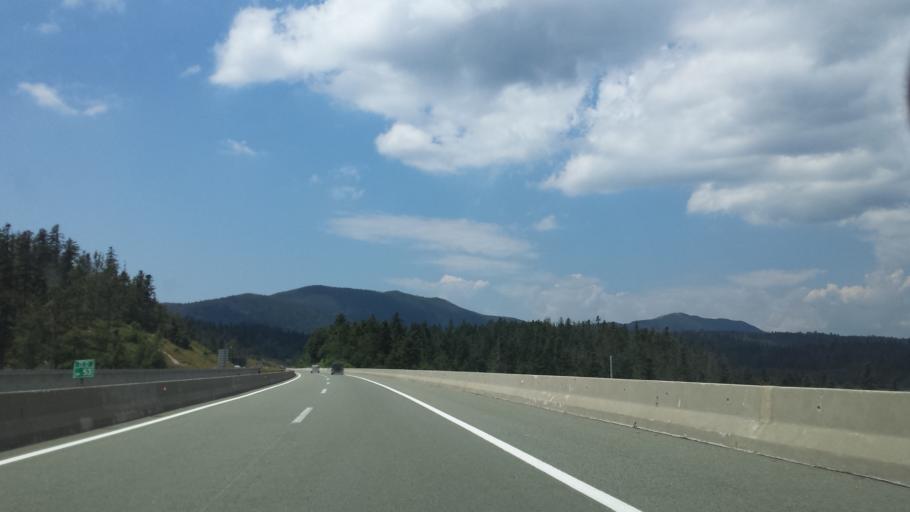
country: HR
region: Primorsko-Goranska
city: Hreljin
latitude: 45.3168
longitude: 14.7112
